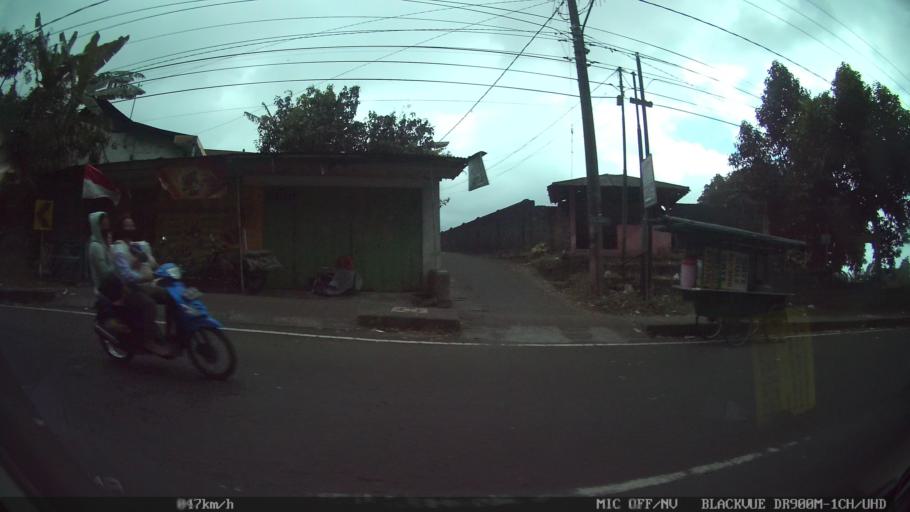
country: ID
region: Bali
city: Bantiran
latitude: -8.3159
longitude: 115.0054
